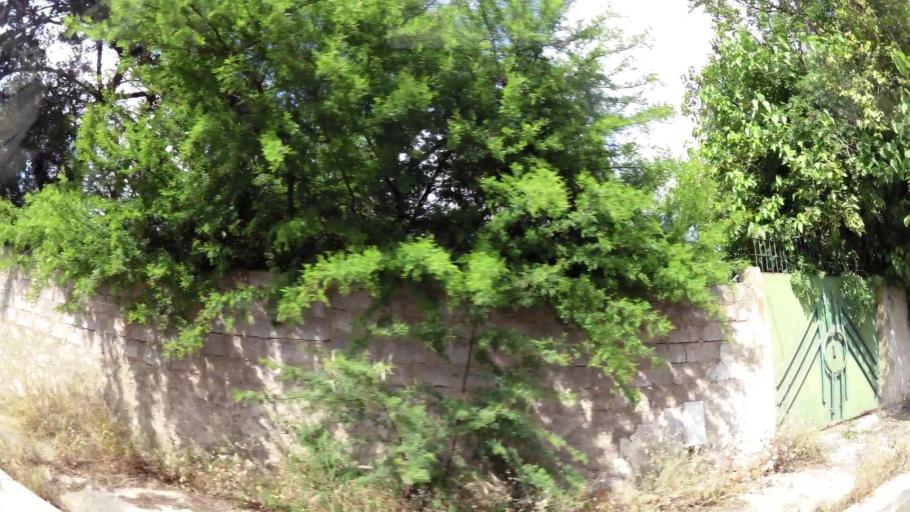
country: MA
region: Rabat-Sale-Zemmour-Zaer
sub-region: Rabat
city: Rabat
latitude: 33.9715
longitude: -6.8520
